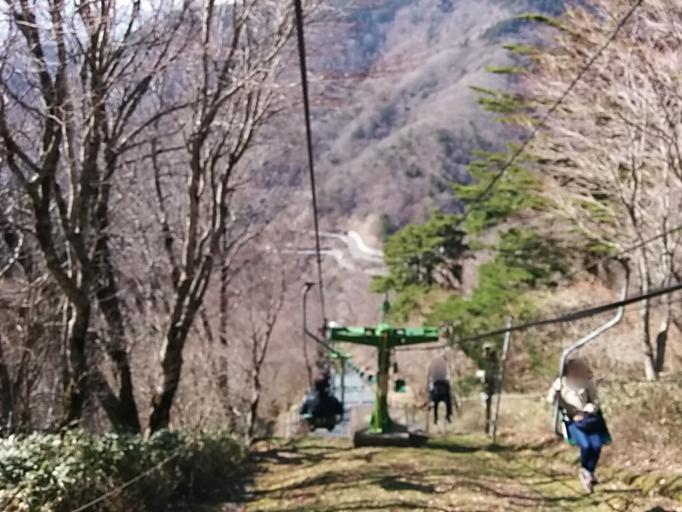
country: JP
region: Tokushima
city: Wakimachi
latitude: 33.8639
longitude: 134.0904
